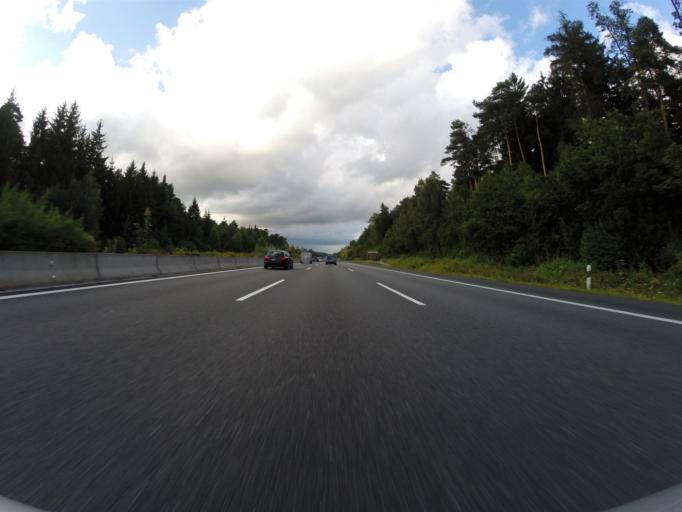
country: DE
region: Bavaria
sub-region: Regierungsbezirk Mittelfranken
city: Neunkirchen am Sand
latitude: 49.5388
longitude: 11.3189
